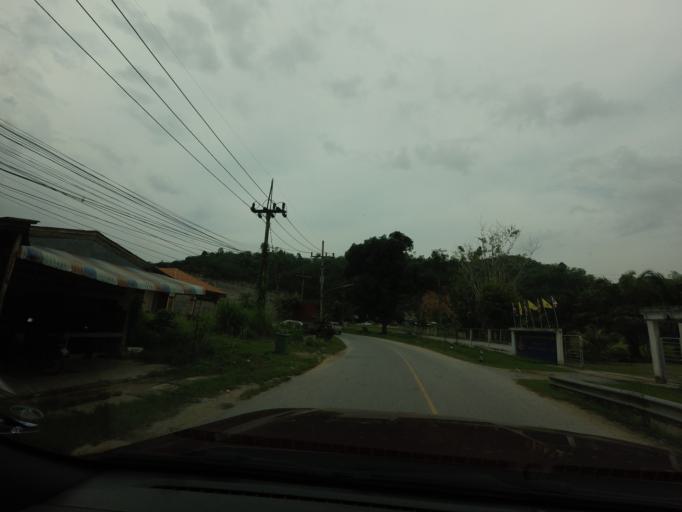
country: TH
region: Yala
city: Than To
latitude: 6.1600
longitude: 101.2778
